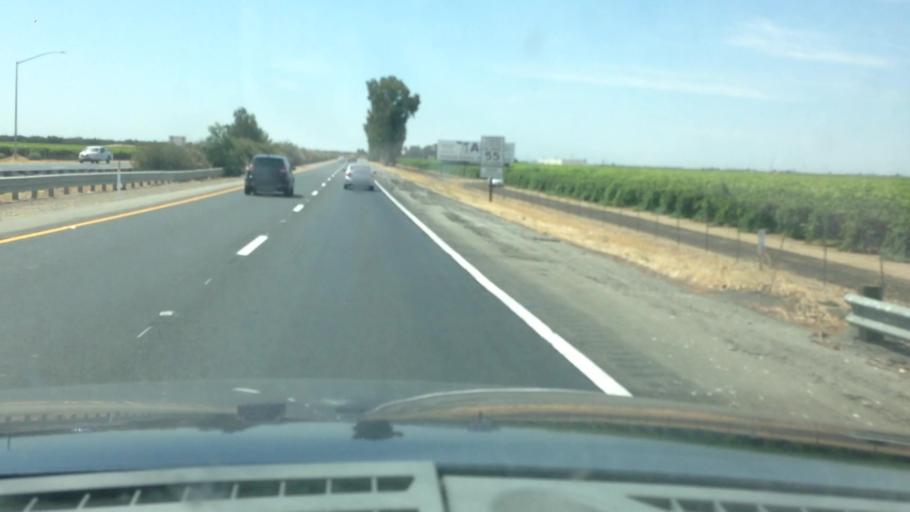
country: US
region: California
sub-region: Tulare County
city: Earlimart
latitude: 35.8316
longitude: -119.2601
